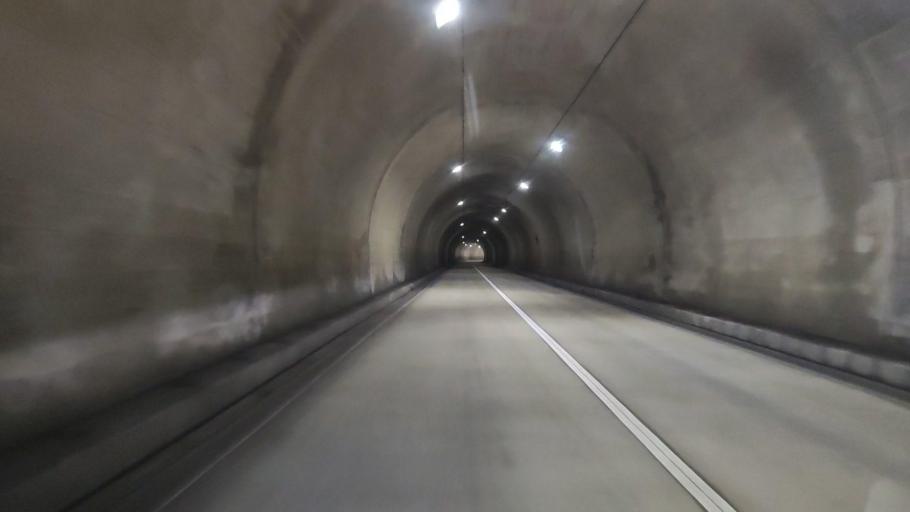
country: JP
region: Wakayama
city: Shingu
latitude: 33.8712
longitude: 135.8566
